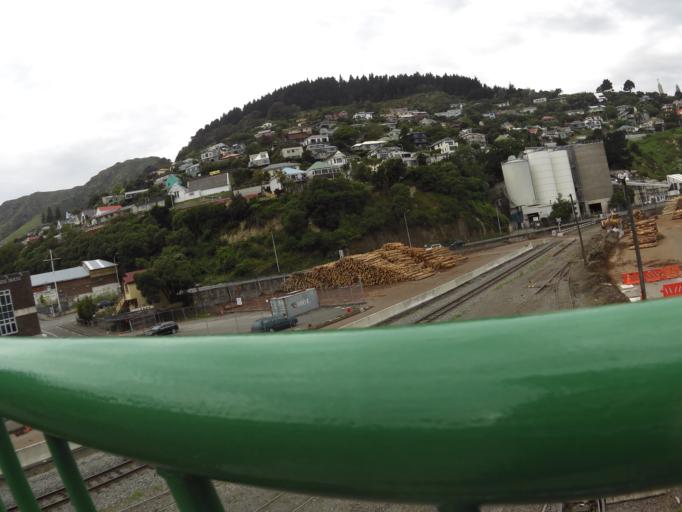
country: NZ
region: Canterbury
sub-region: Christchurch City
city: Christchurch
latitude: -43.6048
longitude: 172.7221
